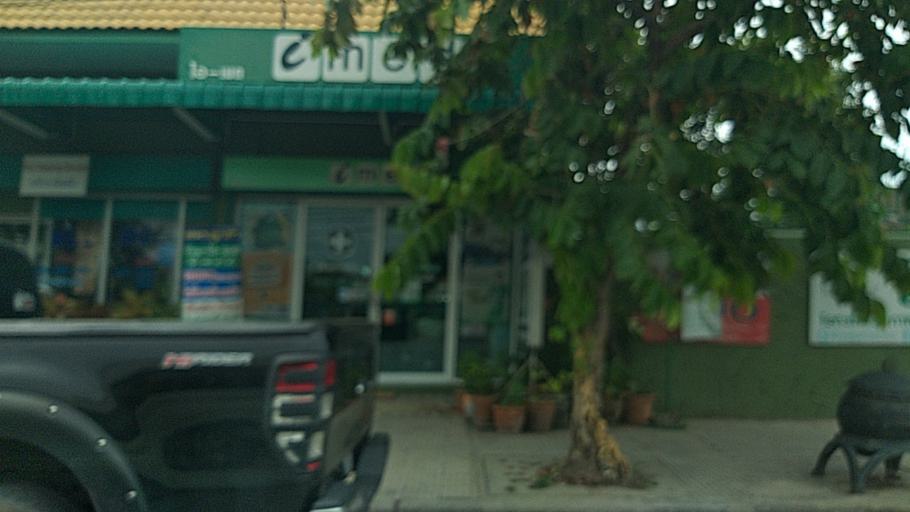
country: TH
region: Bangkok
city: Bang Na
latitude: 13.6808
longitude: 100.6759
